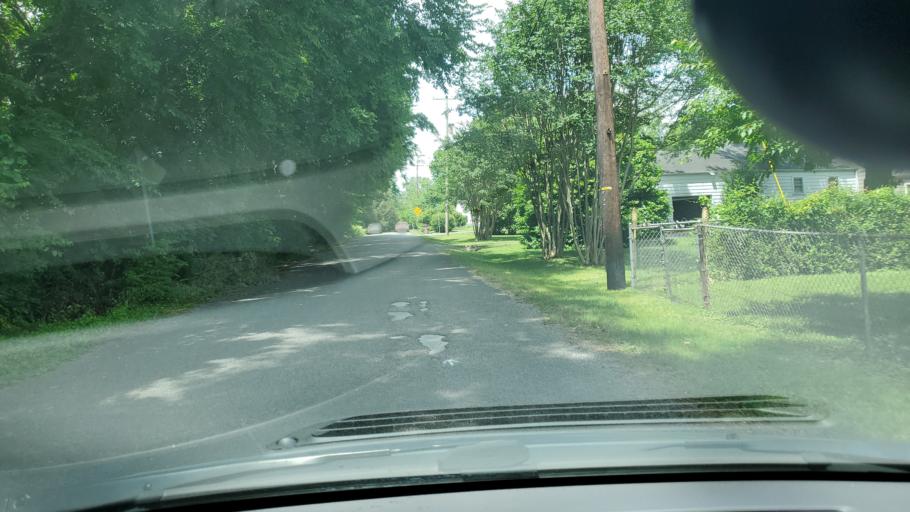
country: US
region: Tennessee
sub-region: Davidson County
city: Nashville
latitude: 36.2281
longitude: -86.7316
